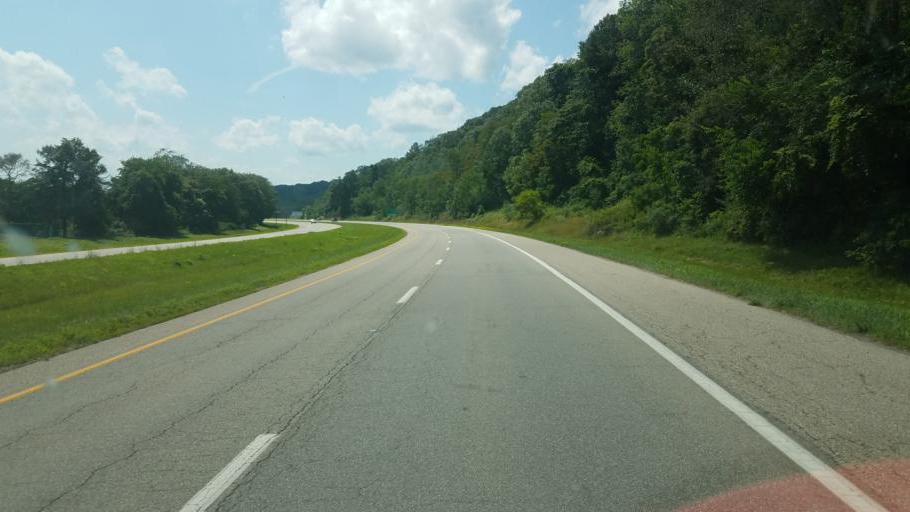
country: US
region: Ohio
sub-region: Coshocton County
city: Coshocton
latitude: 40.3031
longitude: -81.8400
